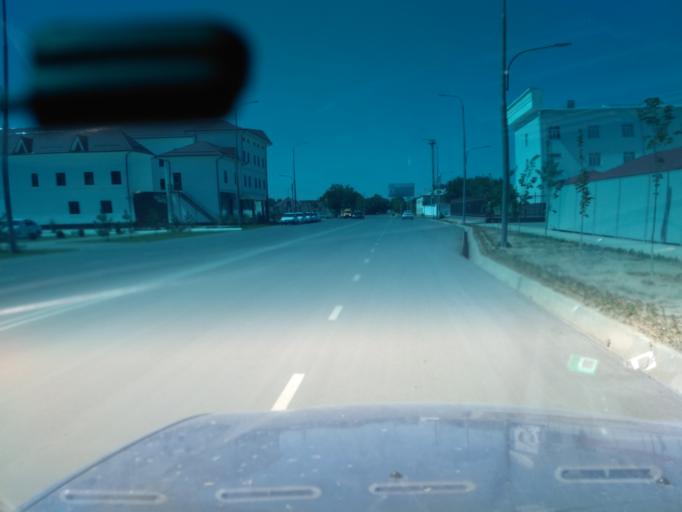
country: UZ
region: Sirdaryo
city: Guliston
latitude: 40.4968
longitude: 68.7709
